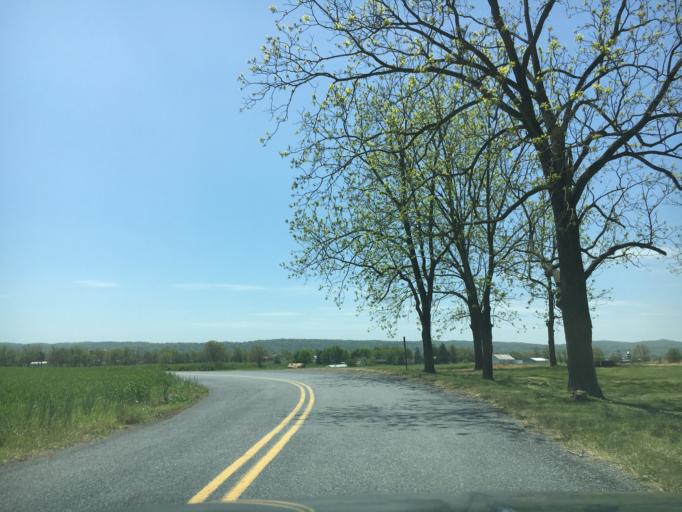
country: US
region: Pennsylvania
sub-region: Berks County
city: Fleetwood
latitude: 40.4852
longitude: -75.8315
